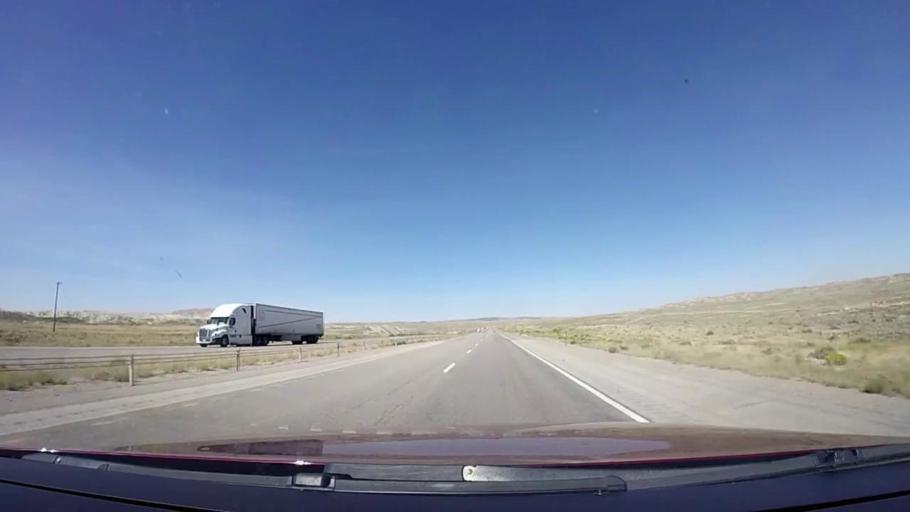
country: US
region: Wyoming
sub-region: Sweetwater County
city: Rock Springs
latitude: 41.6470
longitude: -108.6594
